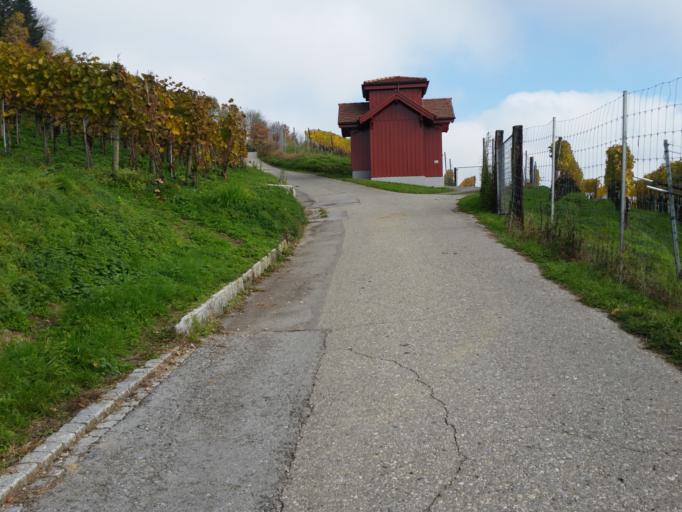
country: CH
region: Appenzell Innerrhoden
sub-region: Appenzell Inner Rhodes
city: Balgach
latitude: 47.4109
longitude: 9.6168
